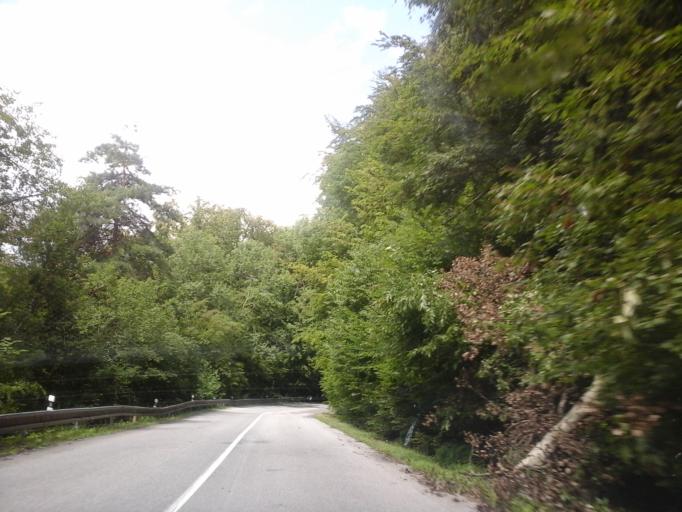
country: SK
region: Kosicky
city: Dobsina
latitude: 48.7112
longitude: 20.3825
